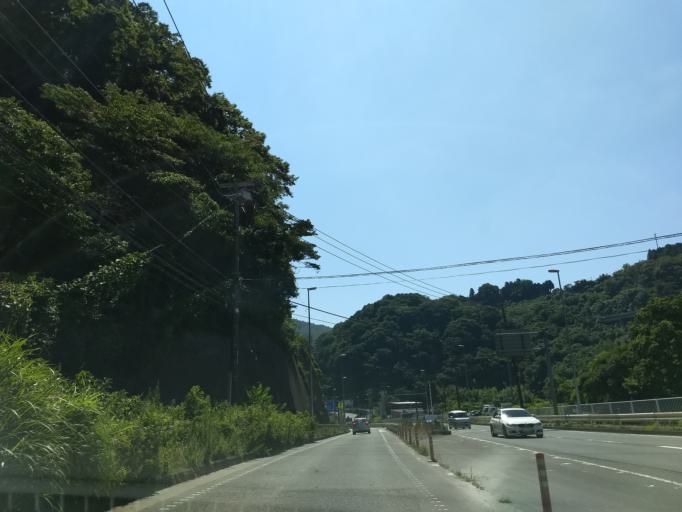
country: JP
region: Shizuoka
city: Gotemba
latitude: 35.3717
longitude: 139.0293
